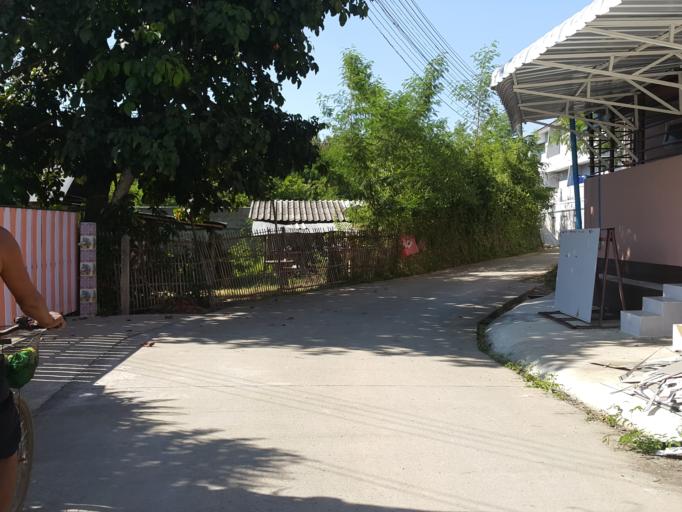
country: TH
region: Chiang Mai
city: Saraphi
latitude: 18.7538
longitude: 99.0551
